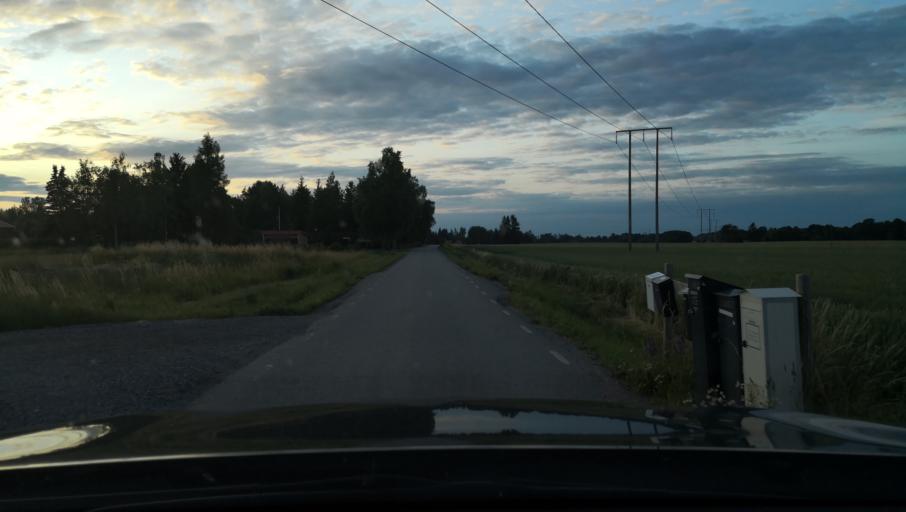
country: SE
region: Uppsala
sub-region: Uppsala Kommun
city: Storvreta
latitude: 60.0229
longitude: 17.6654
